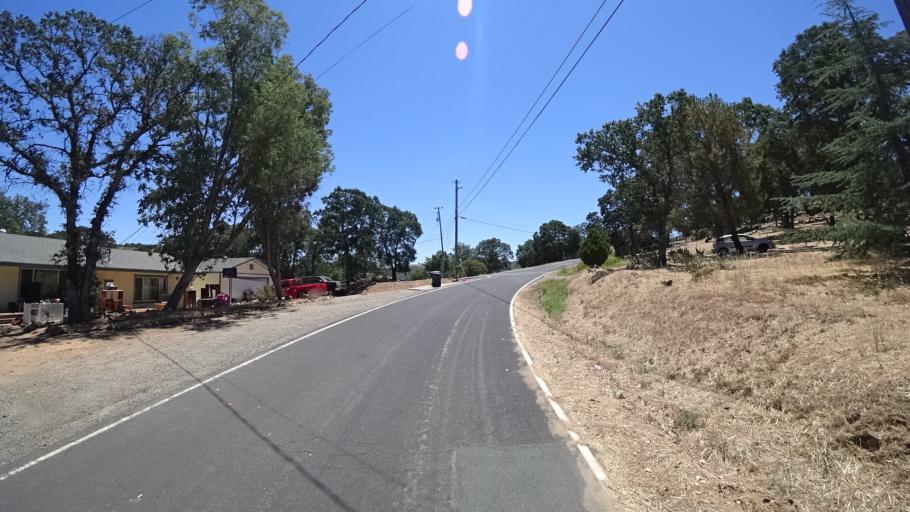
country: US
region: California
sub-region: Calaveras County
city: Rancho Calaveras
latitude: 38.1448
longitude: -120.8382
